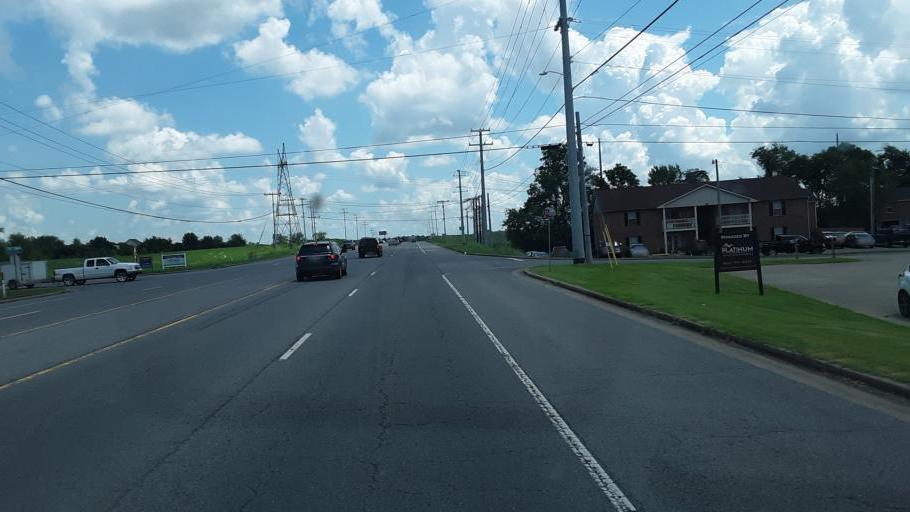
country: US
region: Kentucky
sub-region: Christian County
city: Oak Grove
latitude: 36.6294
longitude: -87.3516
